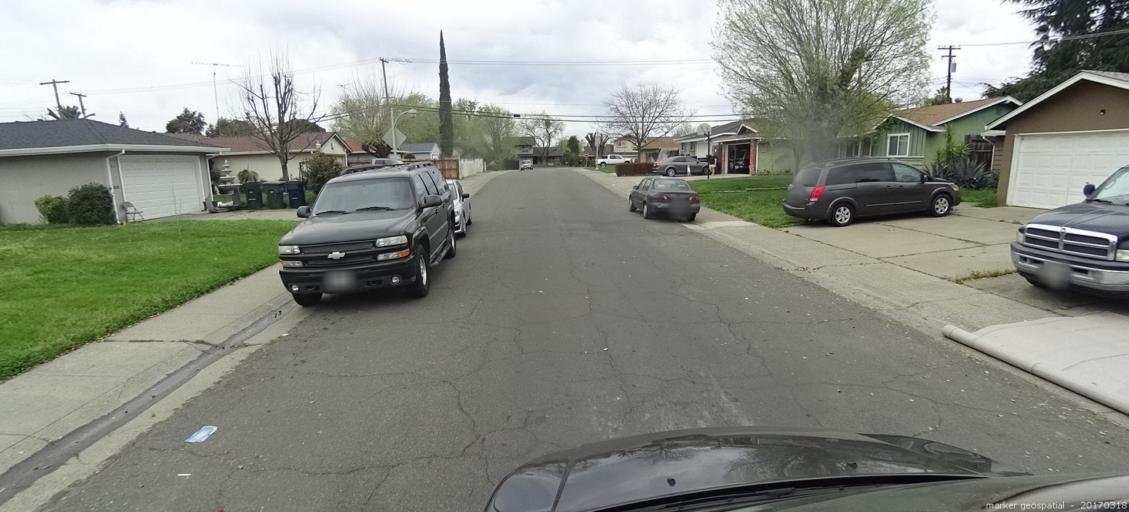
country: US
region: California
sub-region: Sacramento County
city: Parkway
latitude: 38.4846
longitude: -121.4477
